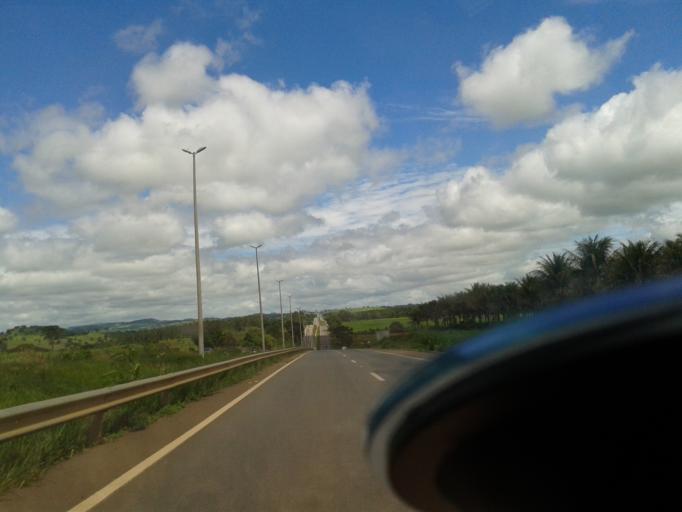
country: BR
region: Goias
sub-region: Goianira
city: Goianira
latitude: -16.4530
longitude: -49.4484
